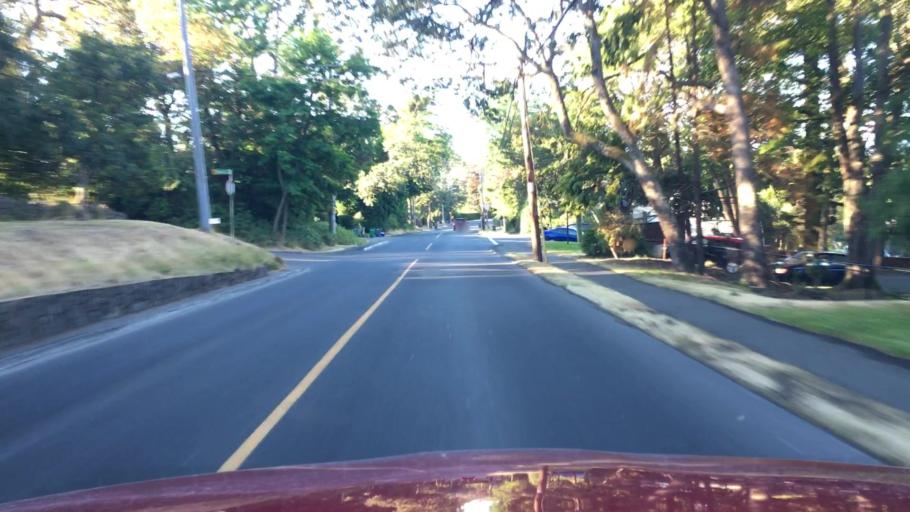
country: CA
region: British Columbia
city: Oak Bay
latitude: 48.4512
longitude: -123.3259
